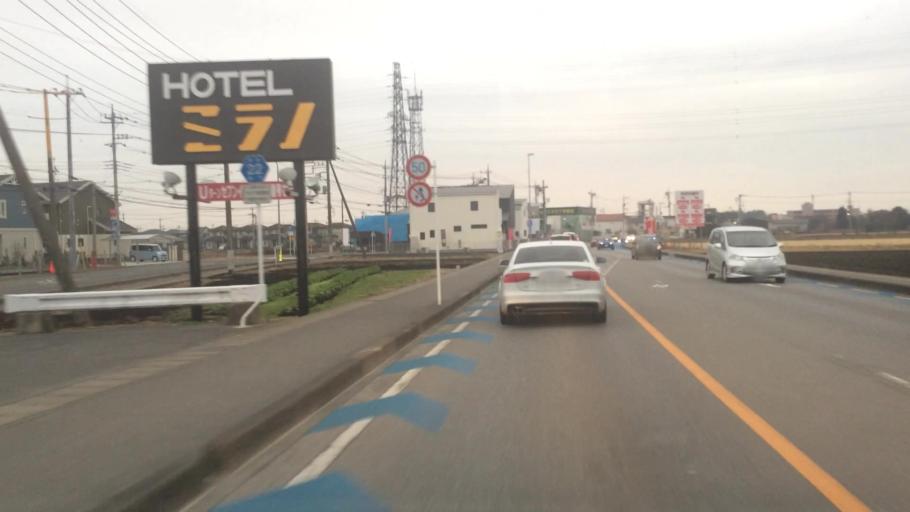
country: JP
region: Tochigi
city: Utsunomiya-shi
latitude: 36.5955
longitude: 139.8530
